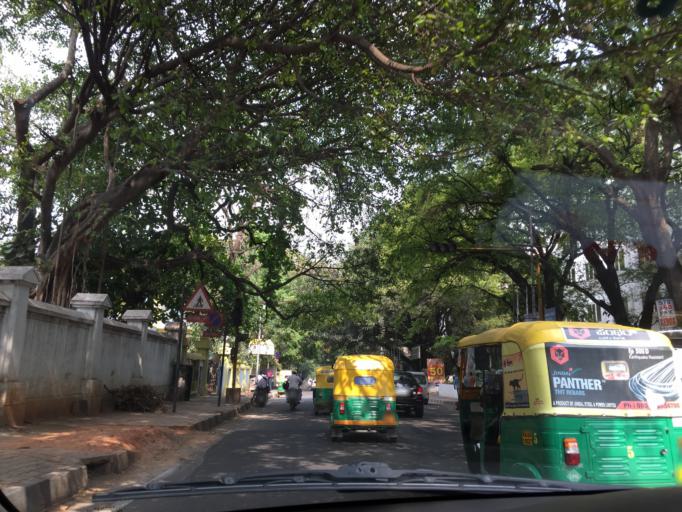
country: IN
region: Karnataka
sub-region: Bangalore Urban
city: Bangalore
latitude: 12.9838
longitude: 77.5941
